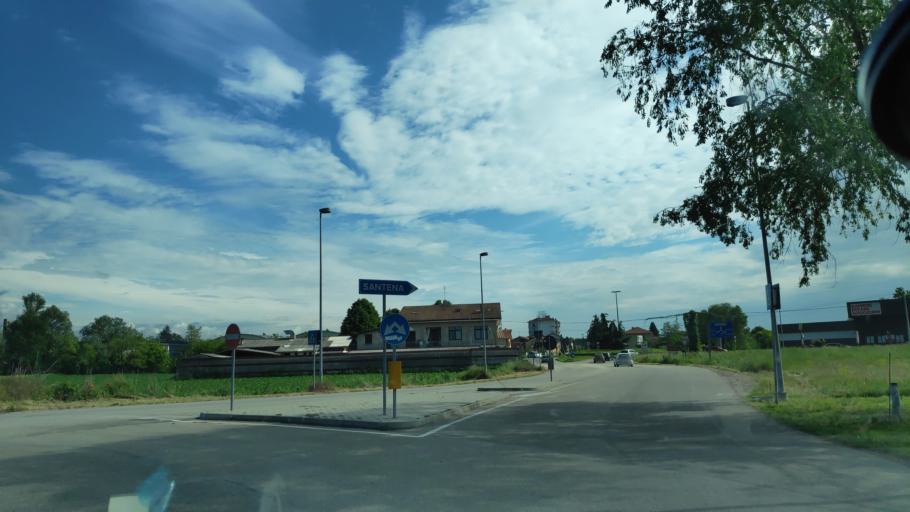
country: IT
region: Piedmont
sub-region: Provincia di Torino
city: Cambiano
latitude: 44.9644
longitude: 7.7780
